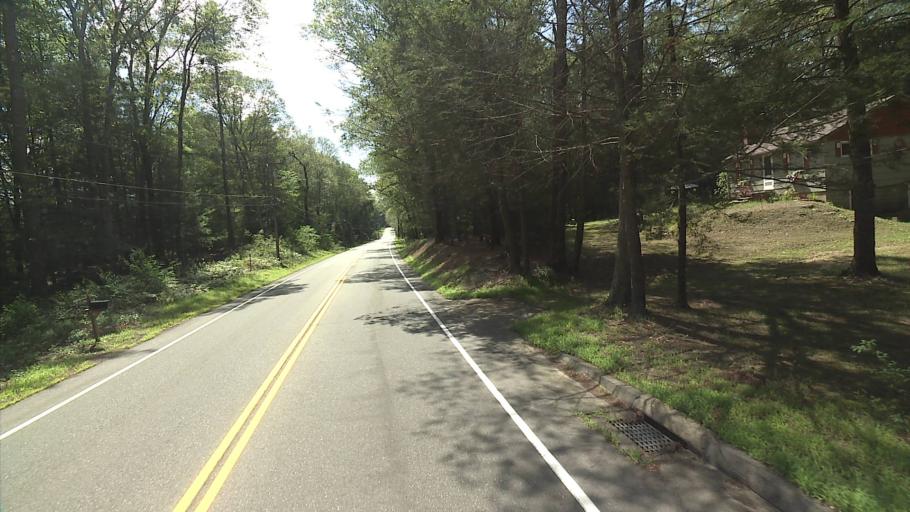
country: US
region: Massachusetts
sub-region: Worcester County
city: Southbridge
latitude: 41.9627
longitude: -72.0792
